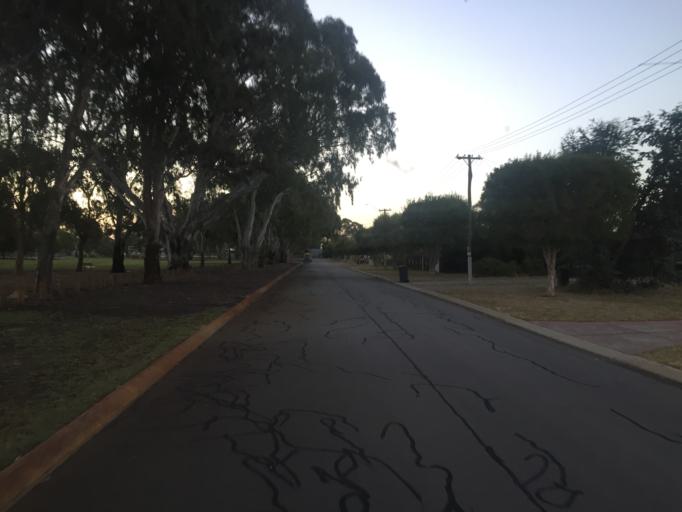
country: AU
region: Western Australia
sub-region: Gosnells
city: Maddington
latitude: -32.0312
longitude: 115.9891
